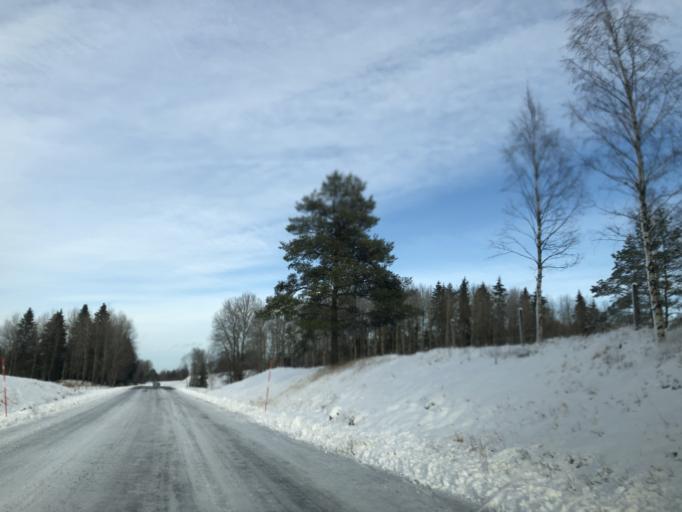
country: SE
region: Vaestra Goetaland
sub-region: Ulricehamns Kommun
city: Ulricehamn
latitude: 57.7990
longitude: 13.5406
